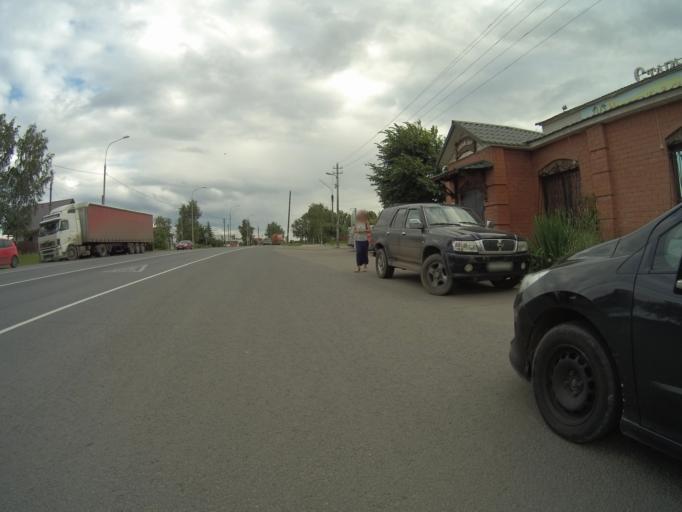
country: RU
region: Vladimir
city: Suzdal'
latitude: 56.3174
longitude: 40.4734
